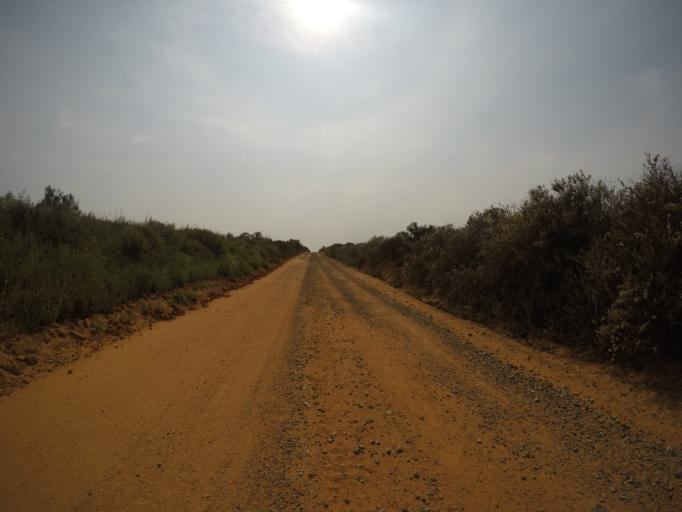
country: ZA
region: Western Cape
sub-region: West Coast District Municipality
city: Malmesbury
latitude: -33.4489
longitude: 18.7463
